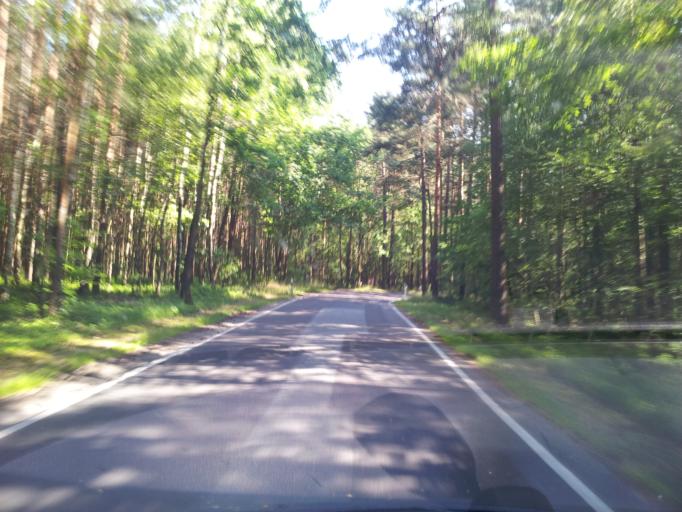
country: DE
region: Saxony
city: Hockendorf
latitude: 51.2393
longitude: 13.9095
